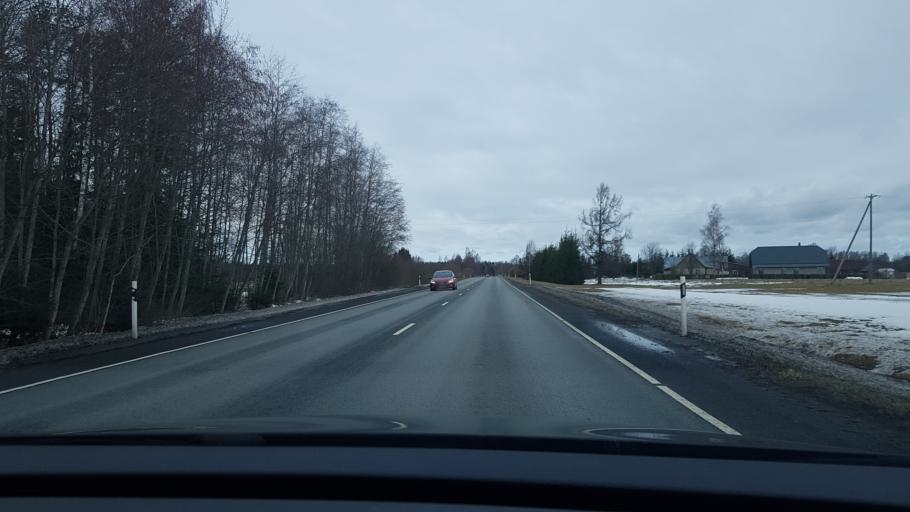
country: EE
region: Paernumaa
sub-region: Paikuse vald
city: Paikuse
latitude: 58.2287
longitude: 24.7007
